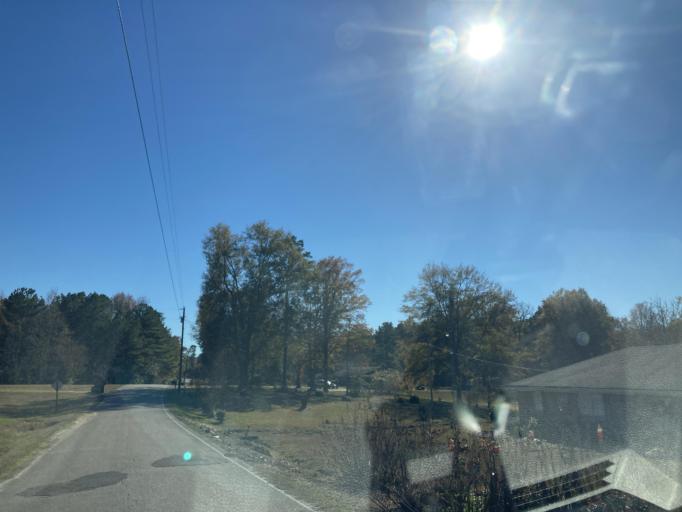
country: US
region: Mississippi
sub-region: Lamar County
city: Sumrall
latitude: 31.2901
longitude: -89.6456
